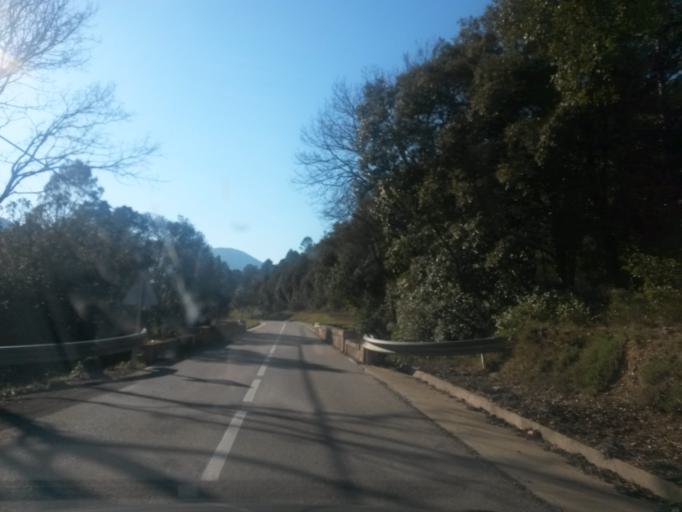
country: ES
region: Catalonia
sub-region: Provincia de Girona
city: Sant Llorenc de la Muga
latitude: 42.3083
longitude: 2.7448
